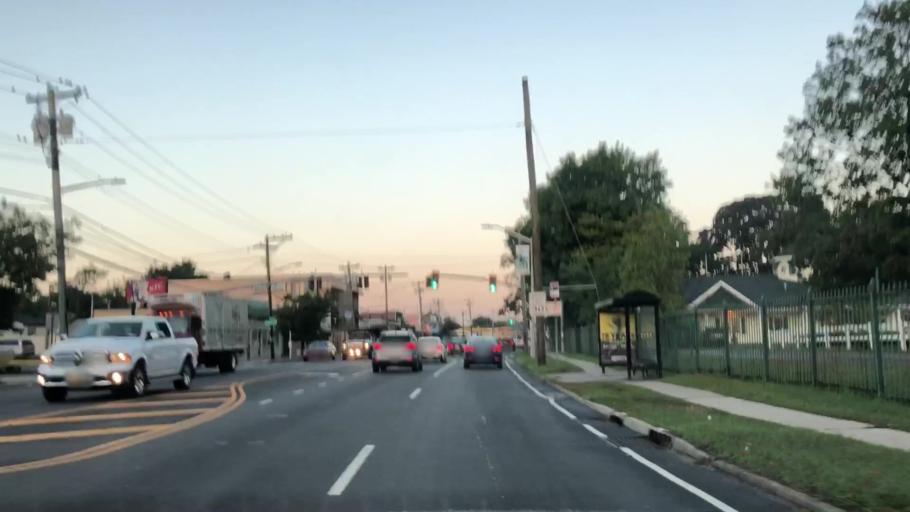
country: US
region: New York
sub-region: Nassau County
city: Elmont
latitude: 40.7081
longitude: -73.7152
